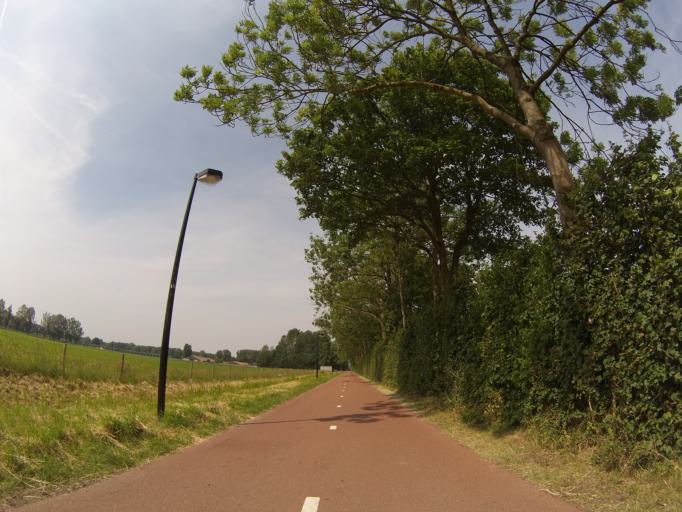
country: NL
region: Utrecht
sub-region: Gemeente Bunnik
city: Bunnik
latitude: 52.0831
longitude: 5.1933
